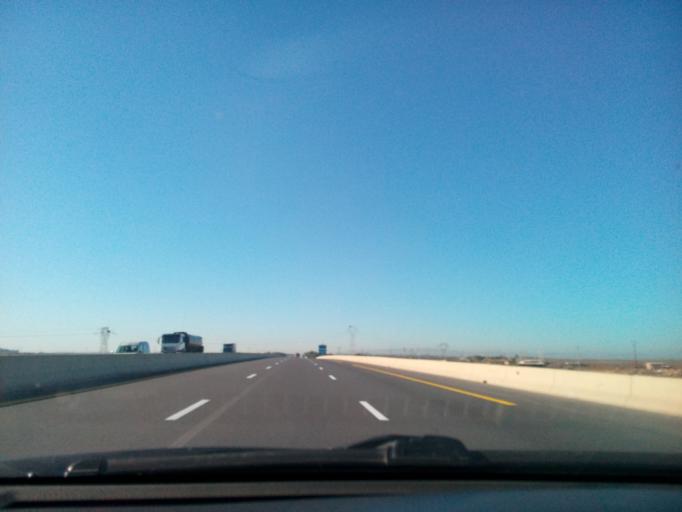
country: DZ
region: Relizane
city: Djidiouia
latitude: 35.9244
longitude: 0.7830
